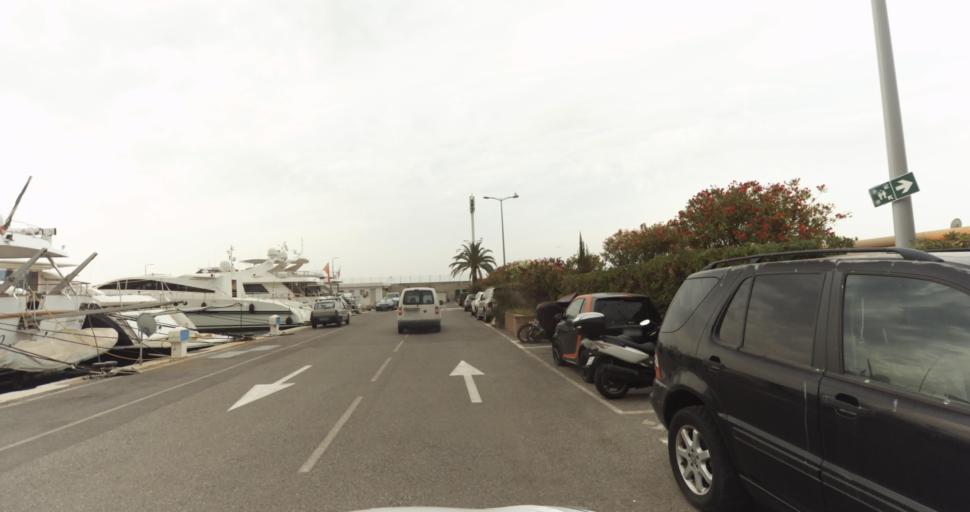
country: FR
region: Provence-Alpes-Cote d'Azur
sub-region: Departement des Alpes-Maritimes
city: Menton
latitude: 43.7824
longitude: 7.5146
